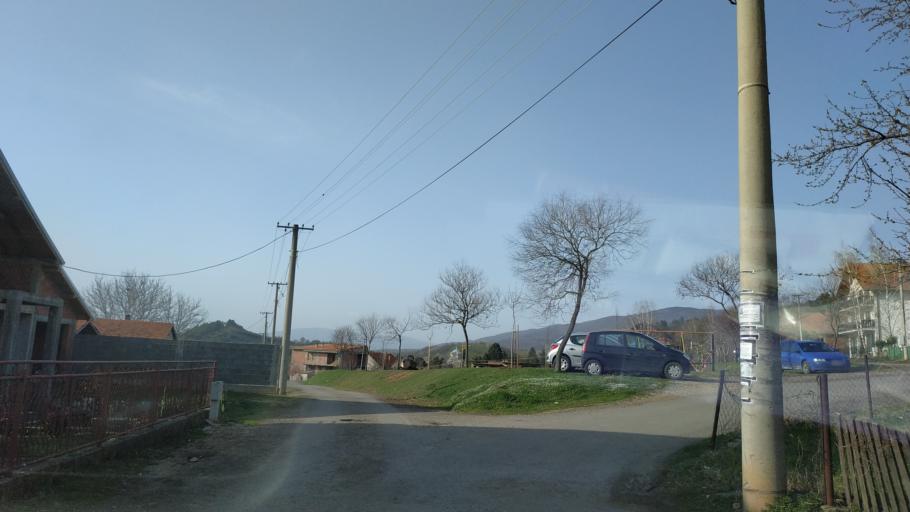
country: RS
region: Central Serbia
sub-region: Nisavski Okrug
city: Aleksinac
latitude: 43.5450
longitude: 21.7161
